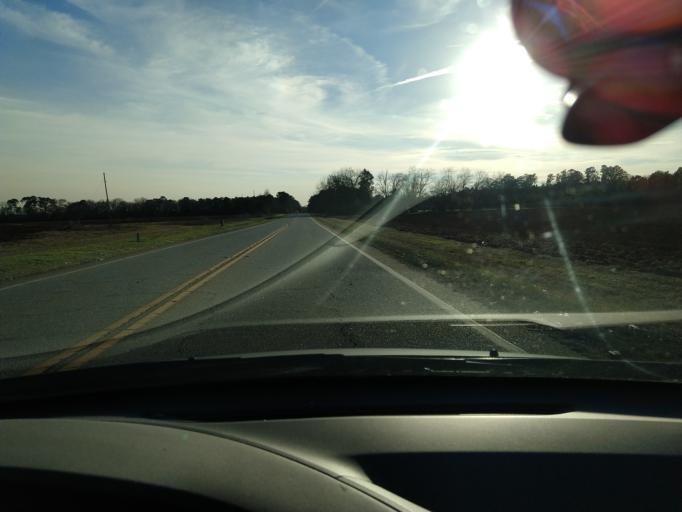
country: US
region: Georgia
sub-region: Sumter County
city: Americus
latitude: 32.1348
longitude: -84.1475
